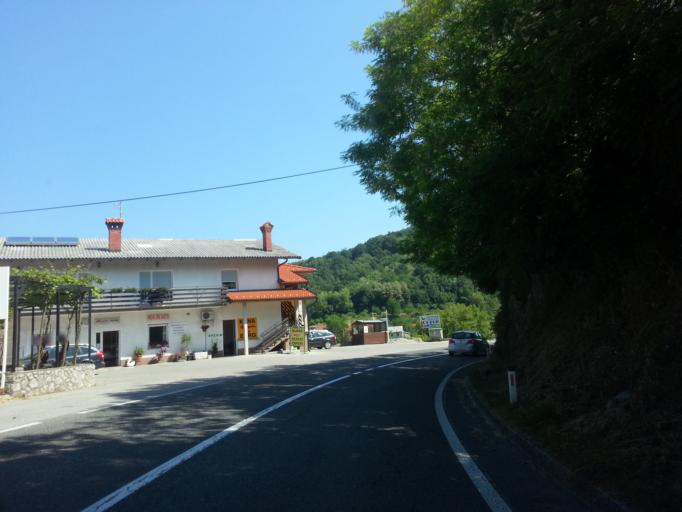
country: SI
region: Ilirska Bistrica
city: Ilirska Bistrica
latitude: 45.5019
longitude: 14.2698
